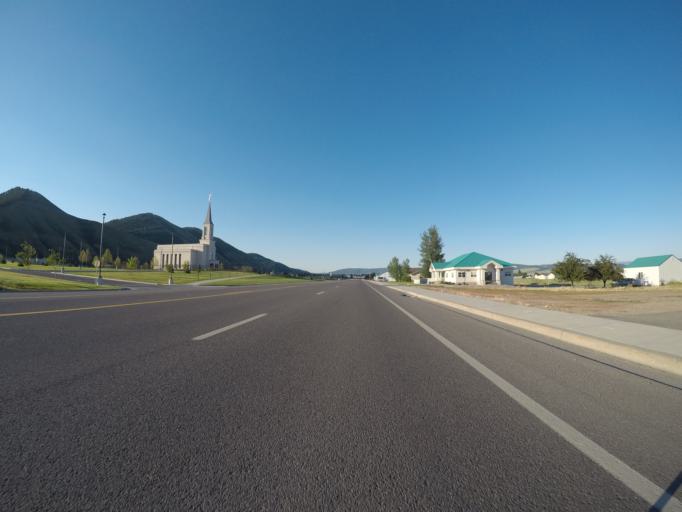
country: US
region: Wyoming
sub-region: Lincoln County
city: Afton
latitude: 42.7133
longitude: -110.9336
